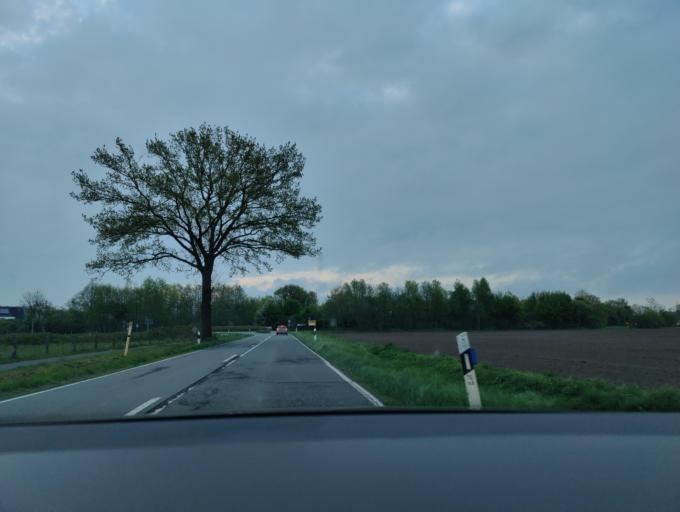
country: DE
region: Lower Saxony
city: Wietmarschen
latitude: 52.4948
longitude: 7.2108
